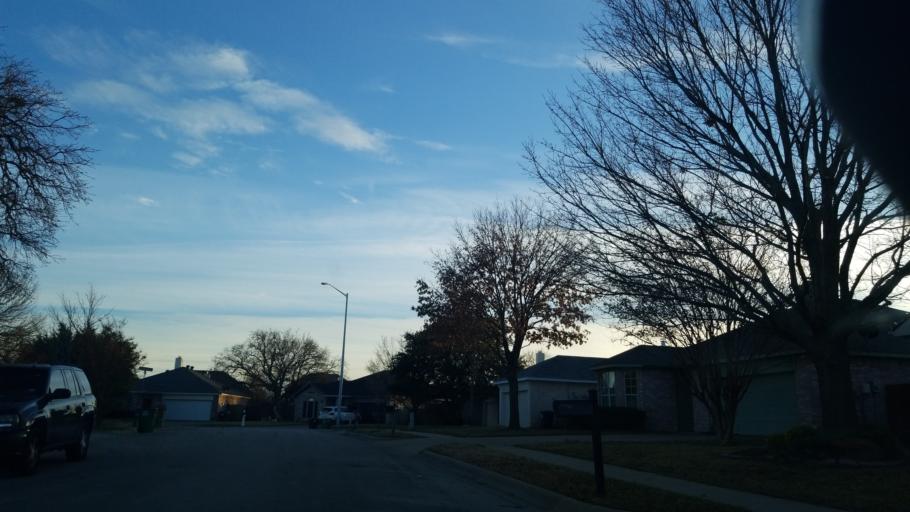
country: US
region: Texas
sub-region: Denton County
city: Corinth
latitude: 33.1595
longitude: -97.1096
